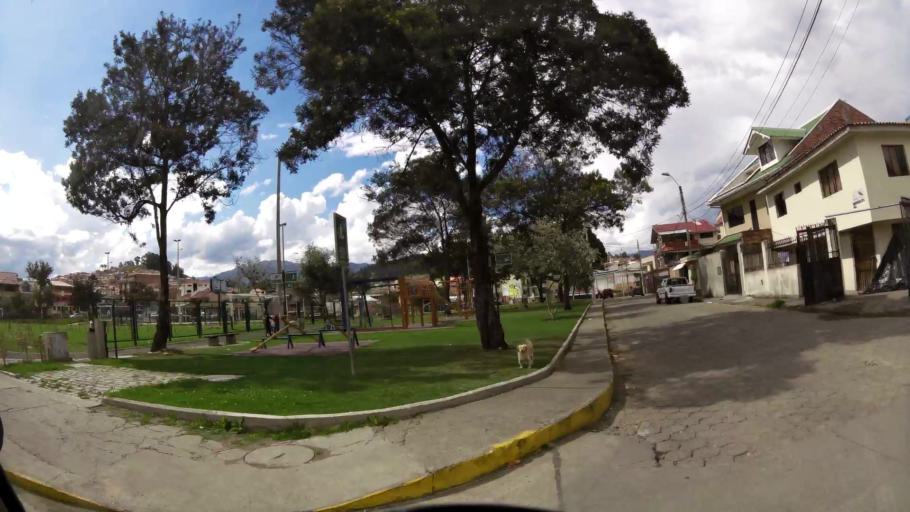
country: EC
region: Azuay
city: Cuenca
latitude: -2.8821
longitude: -78.9837
